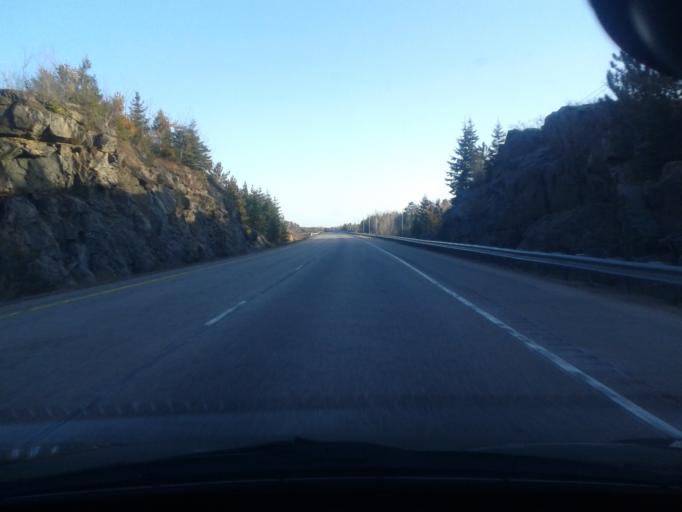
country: CA
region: Ontario
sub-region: Nipissing District
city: North Bay
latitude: 46.2272
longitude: -79.3502
